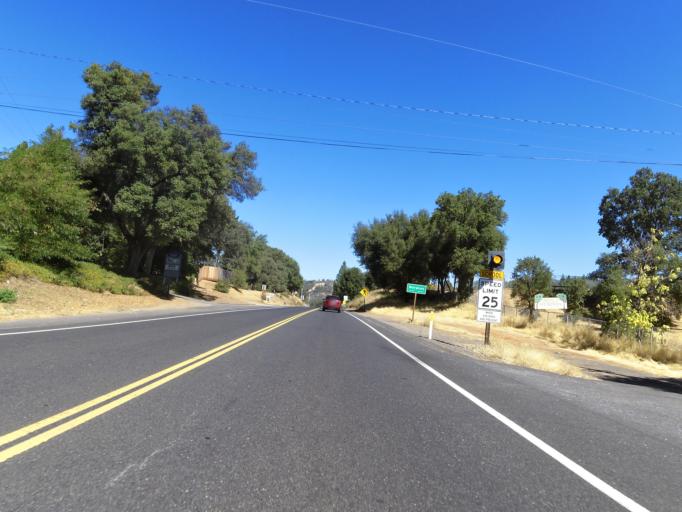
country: US
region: California
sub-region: Calaveras County
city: Murphys
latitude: 38.1311
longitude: -120.4544
